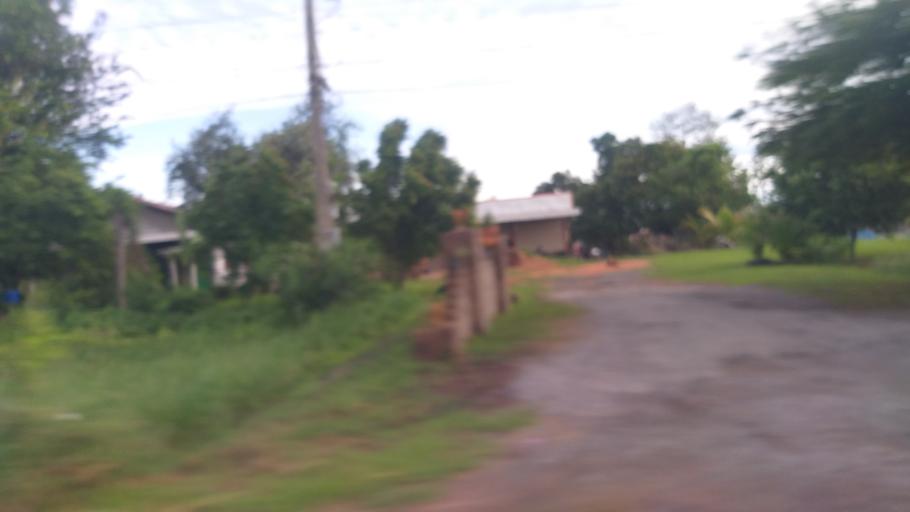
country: TH
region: Chaiyaphum
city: Phu Khiao
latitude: 16.3196
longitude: 102.1989
